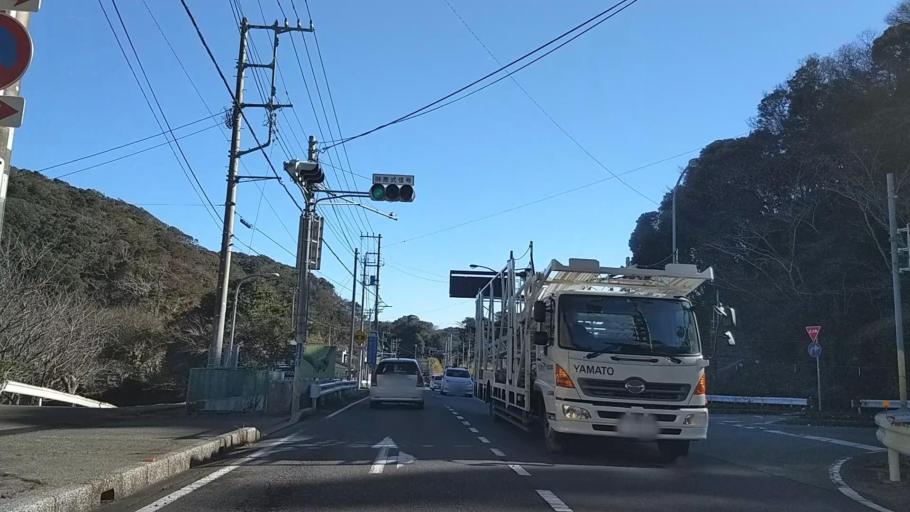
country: JP
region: Chiba
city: Katsuura
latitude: 35.1412
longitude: 140.2697
